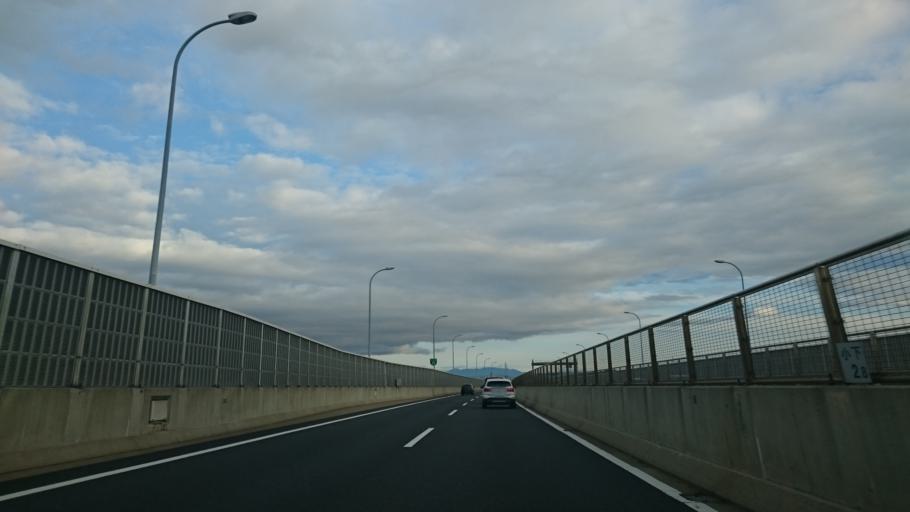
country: JP
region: Aichi
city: Komaki
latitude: 35.2547
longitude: 136.9075
